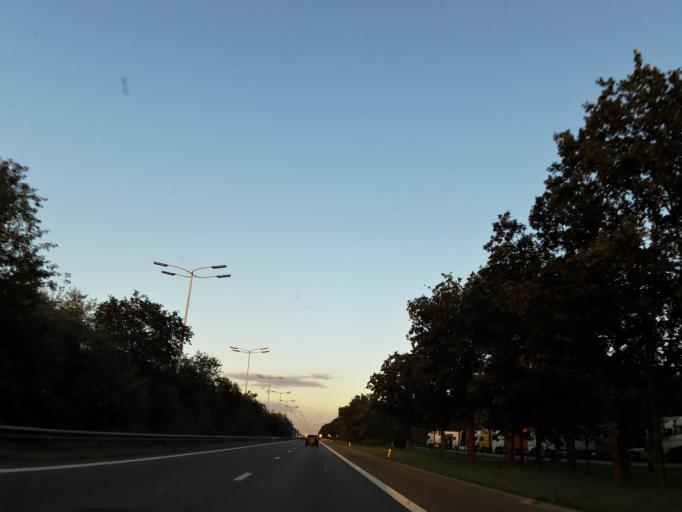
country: BE
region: Flanders
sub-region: Provincie Limburg
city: Zonhoven
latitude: 51.0120
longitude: 5.3329
